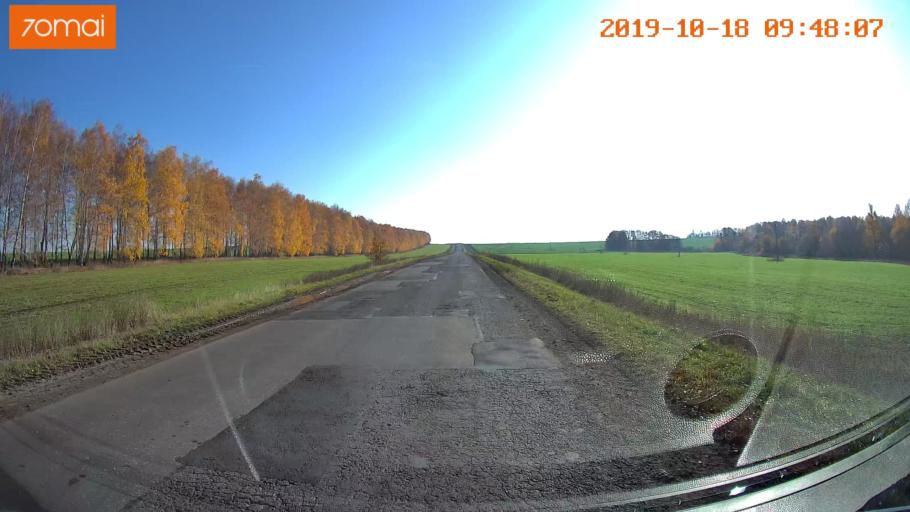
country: RU
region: Tula
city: Kazachka
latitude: 53.3193
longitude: 38.2422
